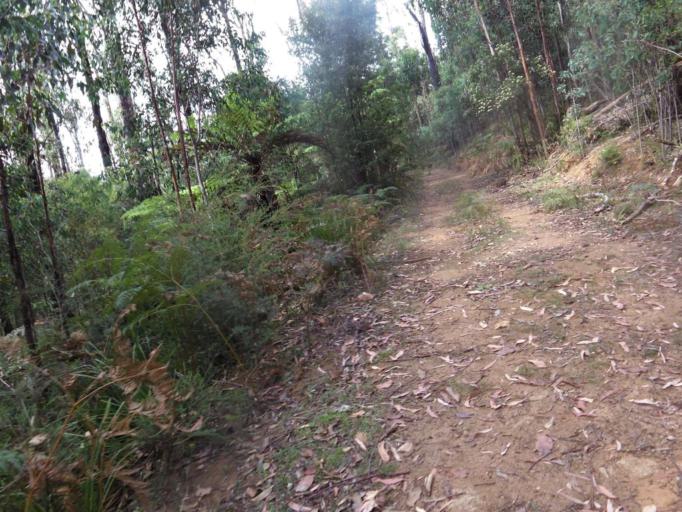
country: AU
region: Victoria
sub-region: Murrindindi
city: Alexandra
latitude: -37.3977
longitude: 145.5796
